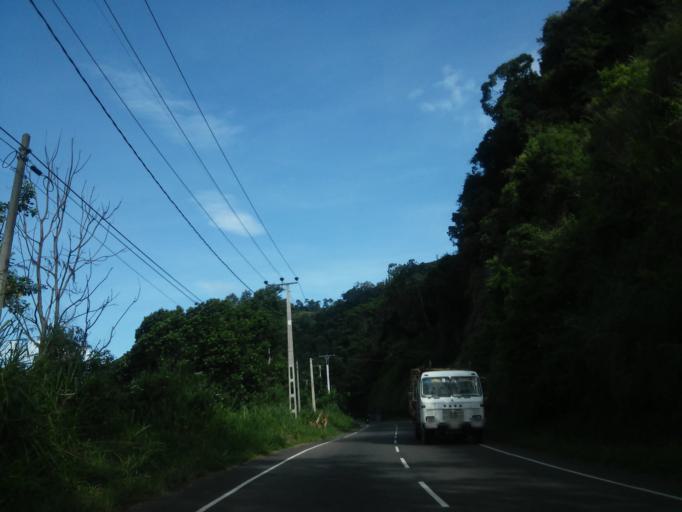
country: LK
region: Uva
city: Haputale
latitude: 6.7649
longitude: 80.8951
